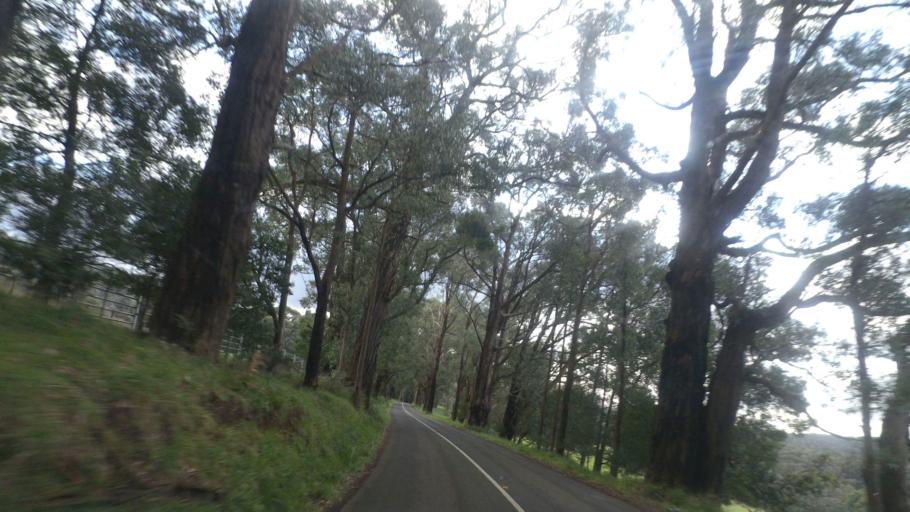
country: AU
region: Victoria
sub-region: Cardinia
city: Emerald
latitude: -37.9046
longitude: 145.4244
